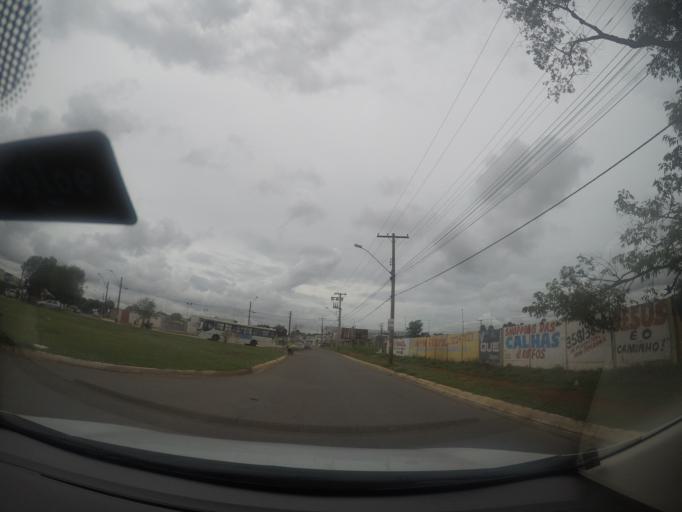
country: BR
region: Goias
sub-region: Trindade
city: Trindade
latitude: -16.6555
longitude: -49.3819
